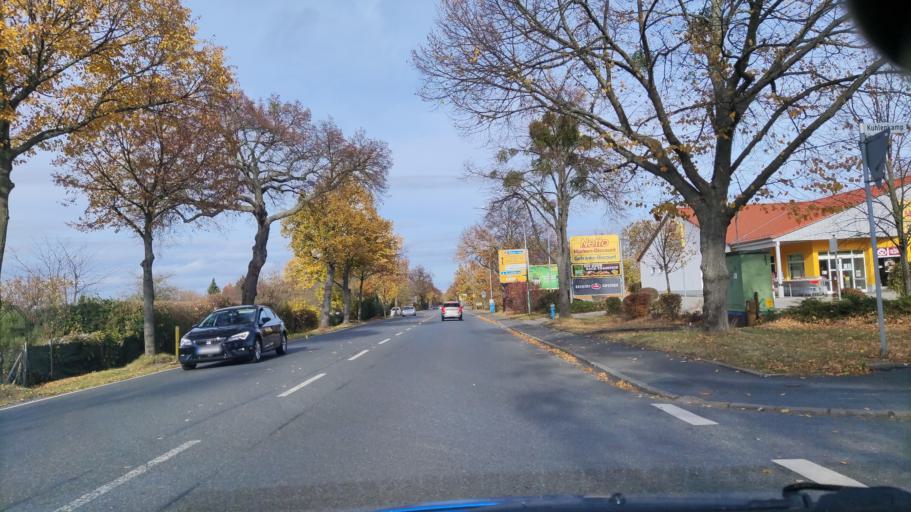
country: DE
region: Lower Saxony
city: Goslar
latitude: 51.9190
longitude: 10.4157
